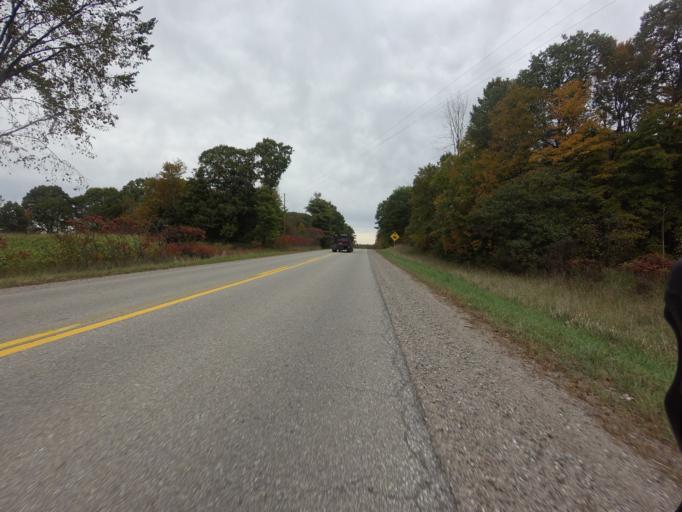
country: CA
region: Ontario
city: Gananoque
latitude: 44.5357
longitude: -76.1444
